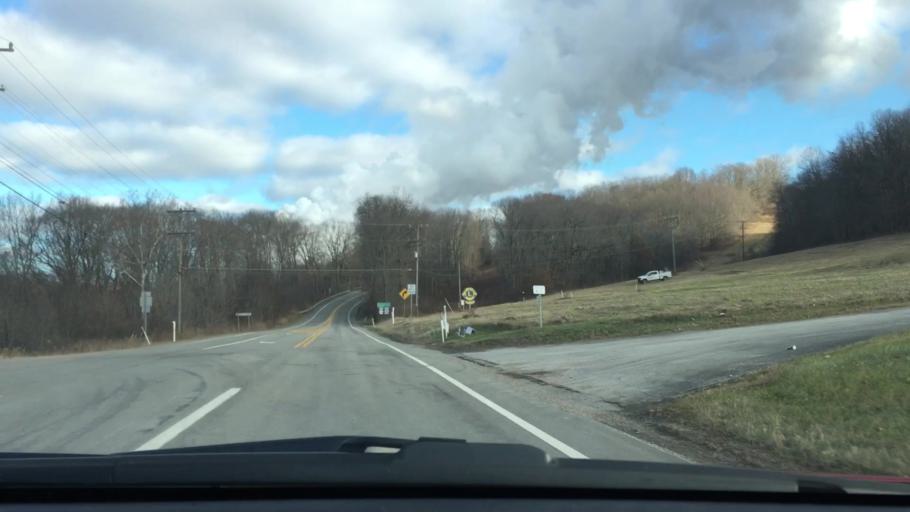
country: US
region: Pennsylvania
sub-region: Westmoreland County
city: Avonmore
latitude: 40.6402
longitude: -79.3525
